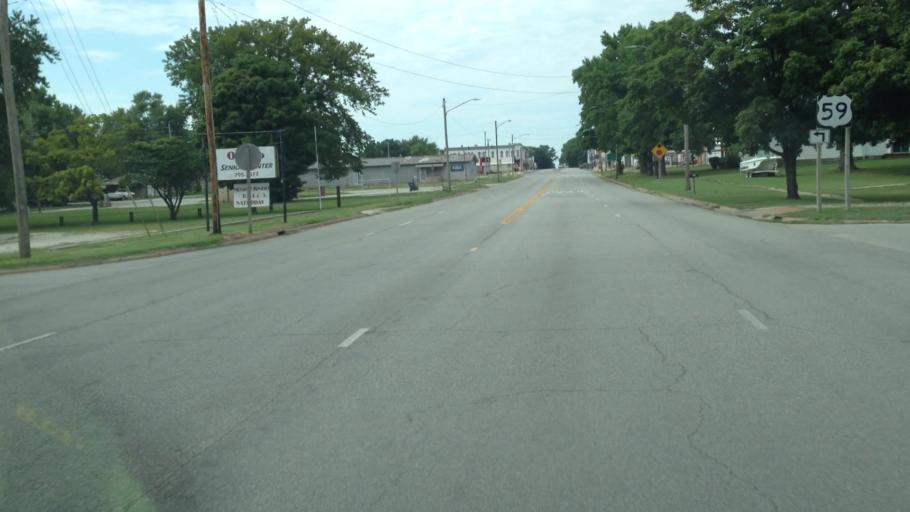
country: US
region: Kansas
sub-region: Labette County
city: Oswego
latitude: 37.1626
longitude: -95.1088
